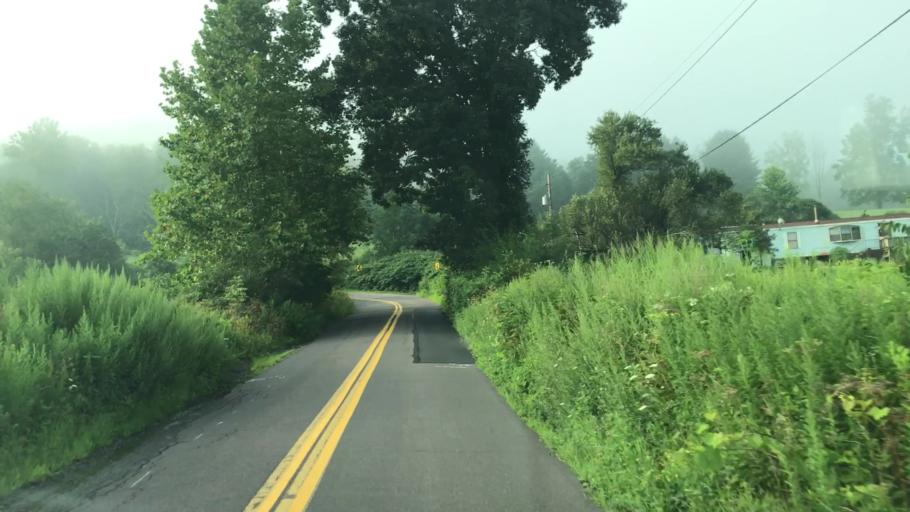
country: US
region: Pennsylvania
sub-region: Wyoming County
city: Factoryville
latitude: 41.6200
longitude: -75.7684
